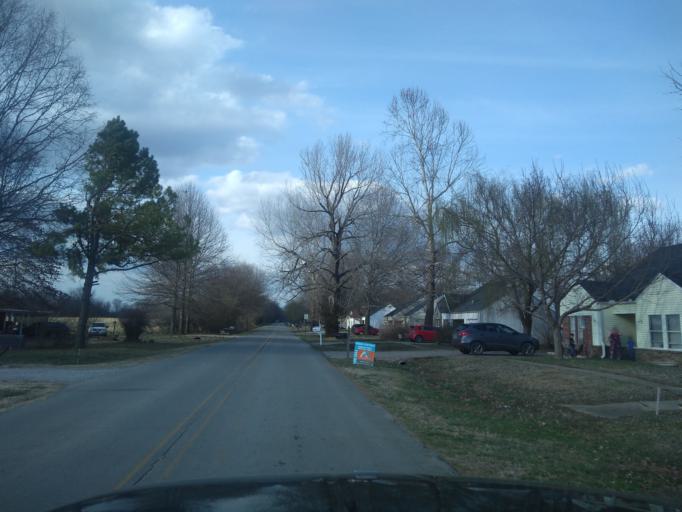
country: US
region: Arkansas
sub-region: Washington County
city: Farmington
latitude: 36.0459
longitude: -94.2405
